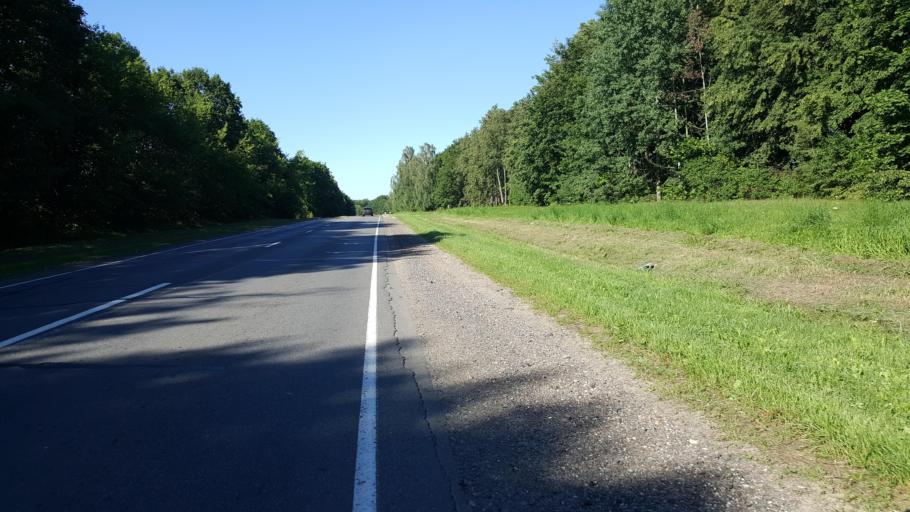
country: BY
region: Brest
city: Charnawchytsy
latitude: 52.2661
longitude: 23.7662
